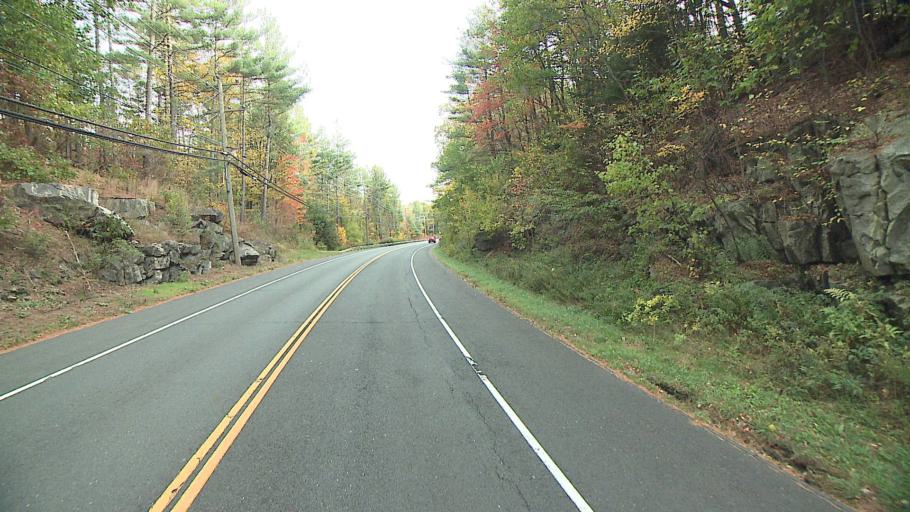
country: US
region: Connecticut
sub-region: Litchfield County
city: New Hartford Center
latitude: 41.9102
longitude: -73.0035
